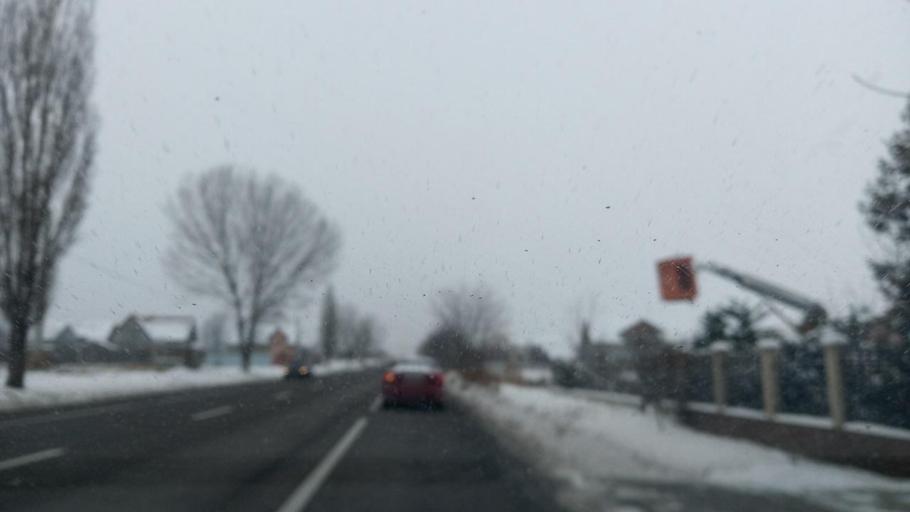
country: RO
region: Bacau
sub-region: Comuna Racaciuni
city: Gheorghe Doja
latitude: 46.3968
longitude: 26.9480
